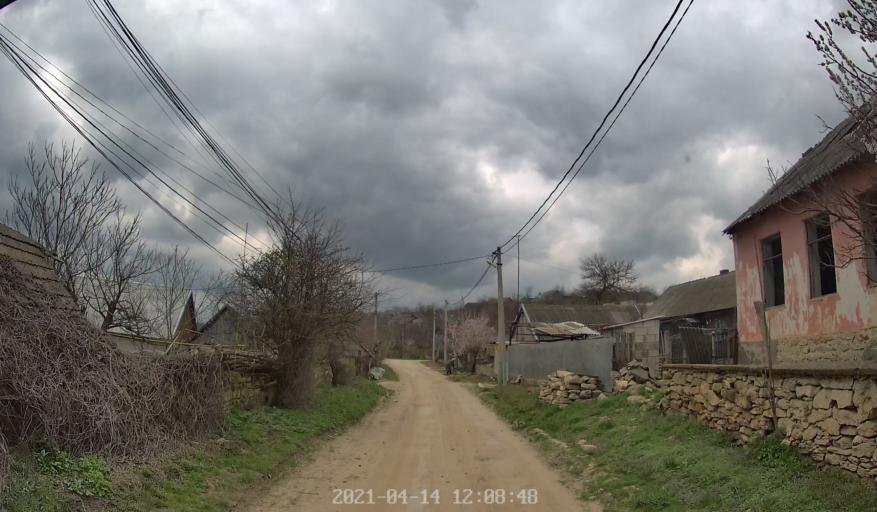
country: MD
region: Criuleni
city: Criuleni
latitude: 47.1709
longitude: 29.2112
